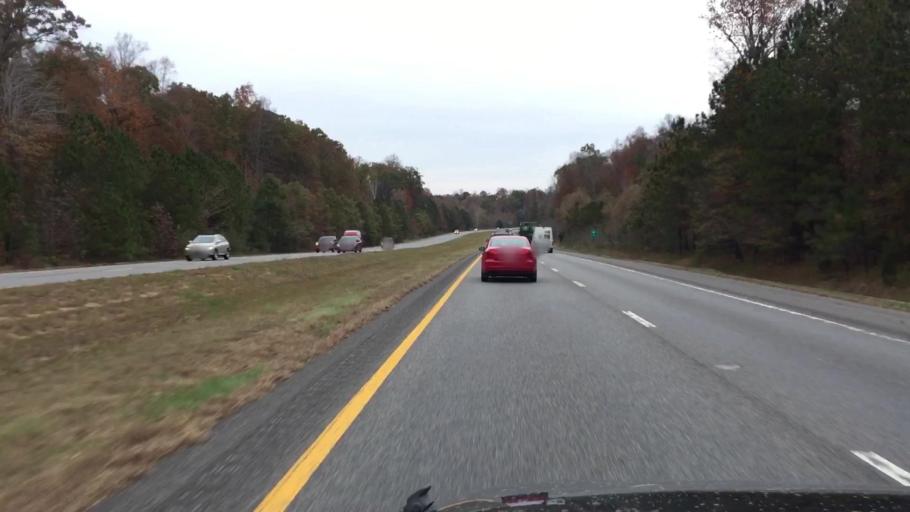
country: US
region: Virginia
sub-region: James City County
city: Williamsburg
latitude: 37.2853
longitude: -76.7531
